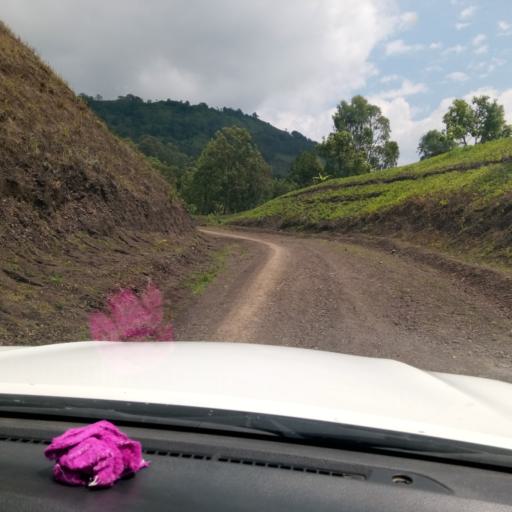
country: ET
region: Southern Nations, Nationalities, and People's Region
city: Arba Minch'
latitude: 6.3136
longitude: 37.3686
